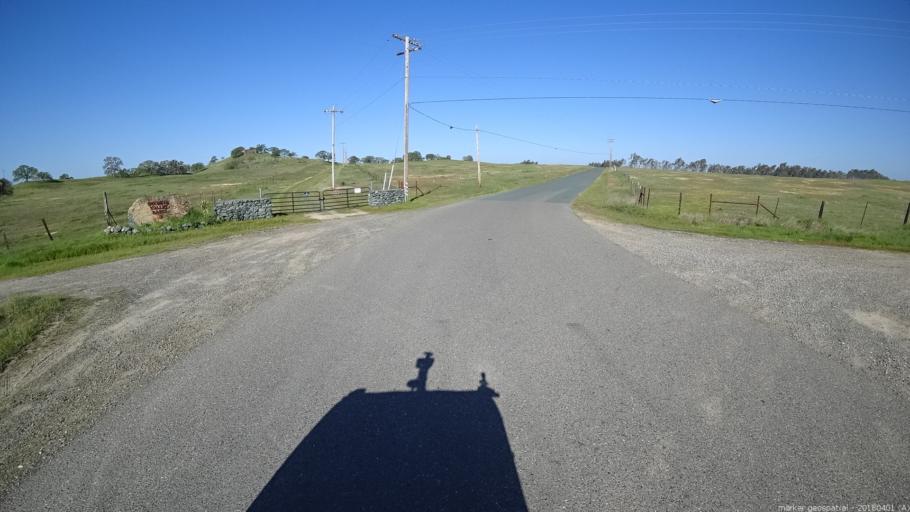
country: US
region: California
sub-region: Sacramento County
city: Rancho Murieta
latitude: 38.4272
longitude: -121.0546
